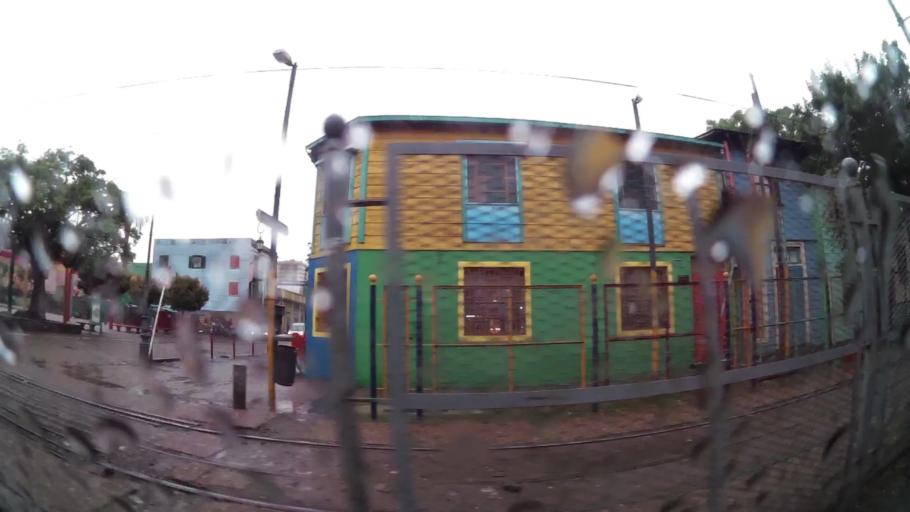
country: AR
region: Buenos Aires
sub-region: Partido de Avellaneda
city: Avellaneda
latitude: -34.6394
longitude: -58.3635
